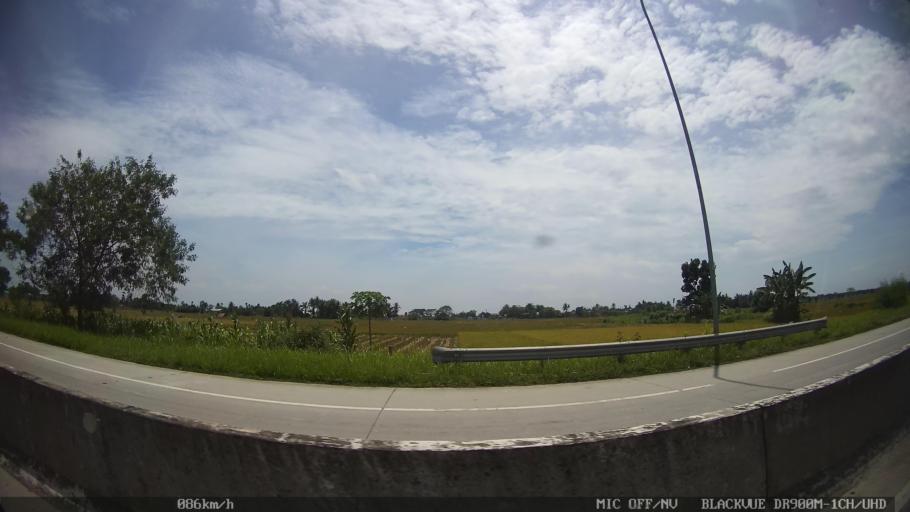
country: ID
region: North Sumatra
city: Perbaungan
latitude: 3.5460
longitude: 98.8901
